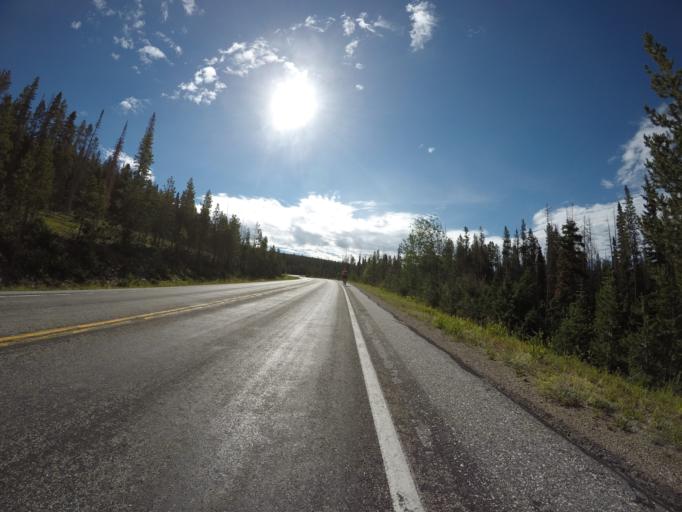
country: US
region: Wyoming
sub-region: Carbon County
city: Saratoga
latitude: 41.3258
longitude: -106.4670
